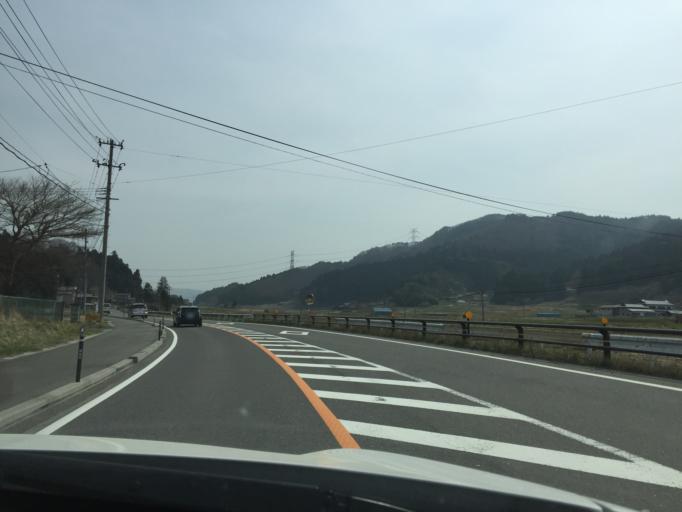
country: JP
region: Fukushima
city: Ishikawa
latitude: 37.1325
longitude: 140.4945
